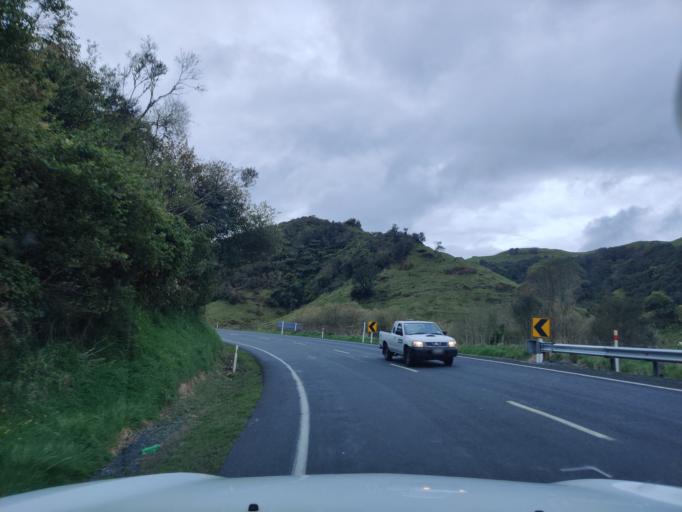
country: NZ
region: Waikato
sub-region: Otorohanga District
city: Otorohanga
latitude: -38.5150
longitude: 175.2088
